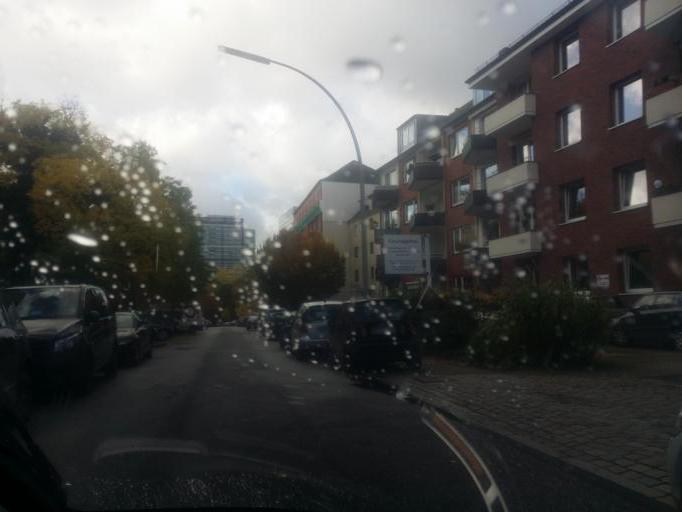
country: DE
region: Hamburg
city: Borgfelde
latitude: 53.5551
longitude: 10.0300
